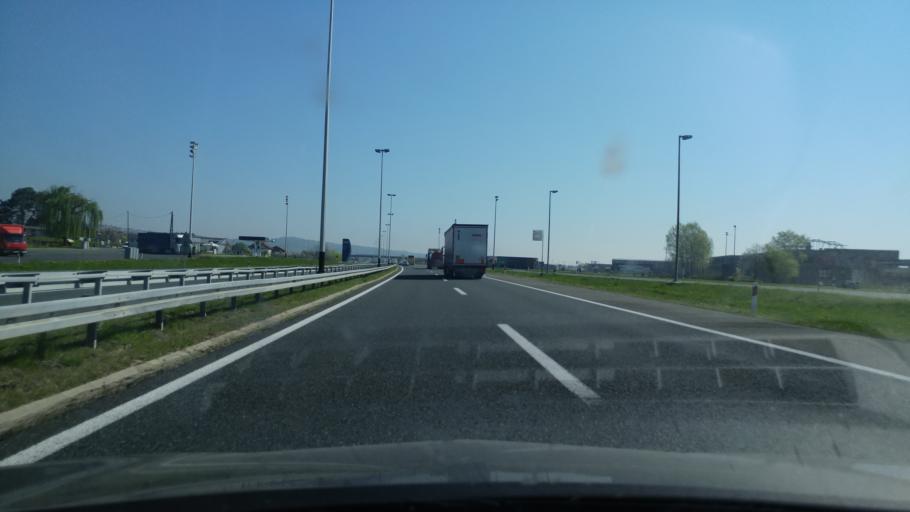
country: HR
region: Brodsko-Posavska
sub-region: Grad Slavonski Brod
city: Slavonski Brod
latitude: 45.1799
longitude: 18.0039
